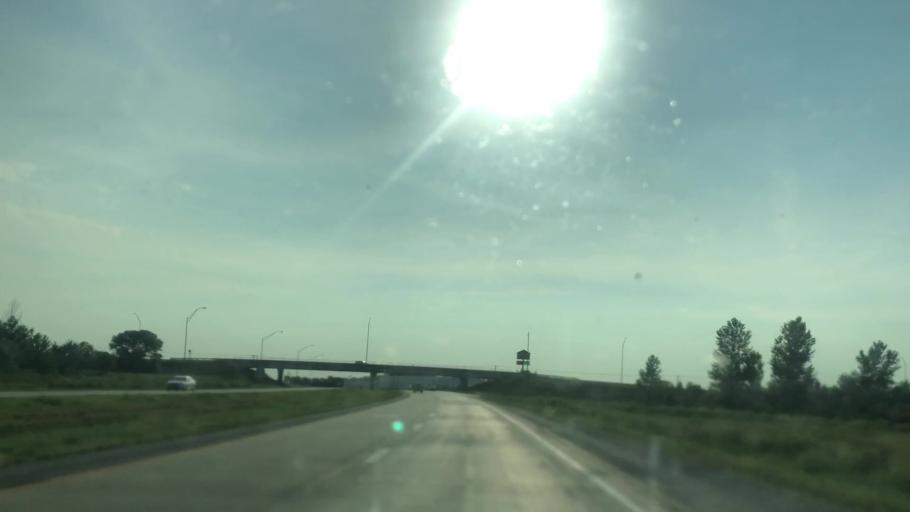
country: US
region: Iowa
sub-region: Story County
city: Nevada
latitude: 42.0082
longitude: -93.4318
